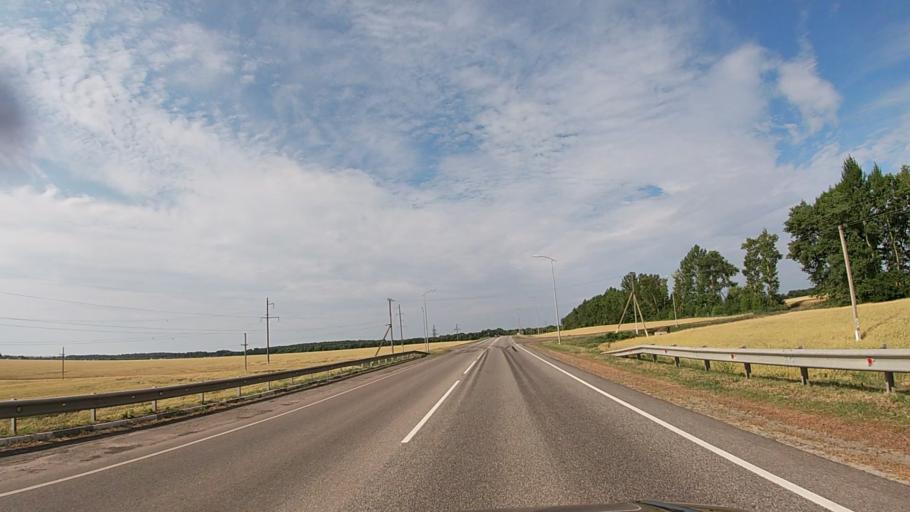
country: RU
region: Belgorod
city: Proletarskiy
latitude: 50.8091
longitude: 35.7459
